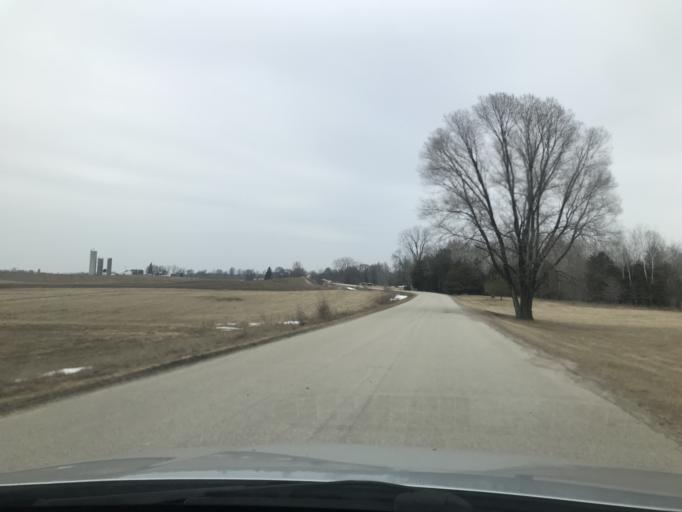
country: US
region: Wisconsin
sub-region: Marinette County
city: Peshtigo
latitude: 45.0288
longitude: -87.8694
